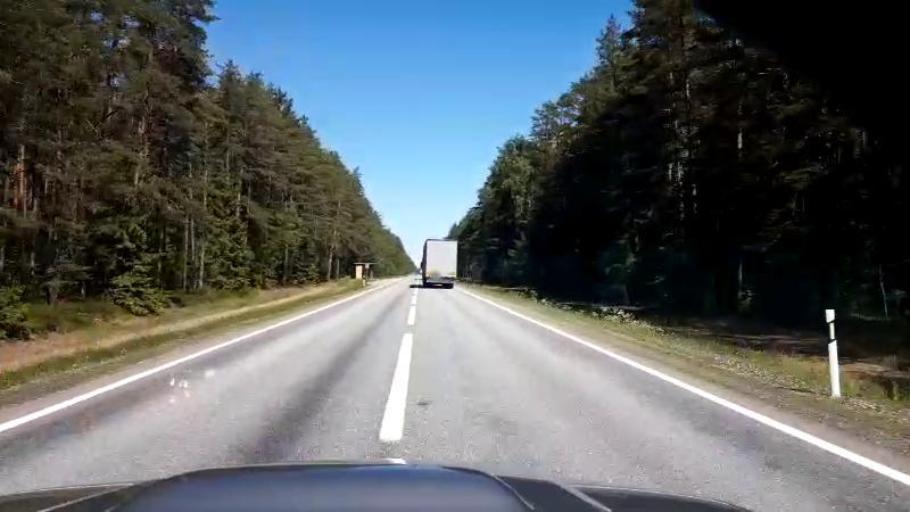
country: LV
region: Salacgrivas
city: Salacgriva
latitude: 57.5405
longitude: 24.4318
